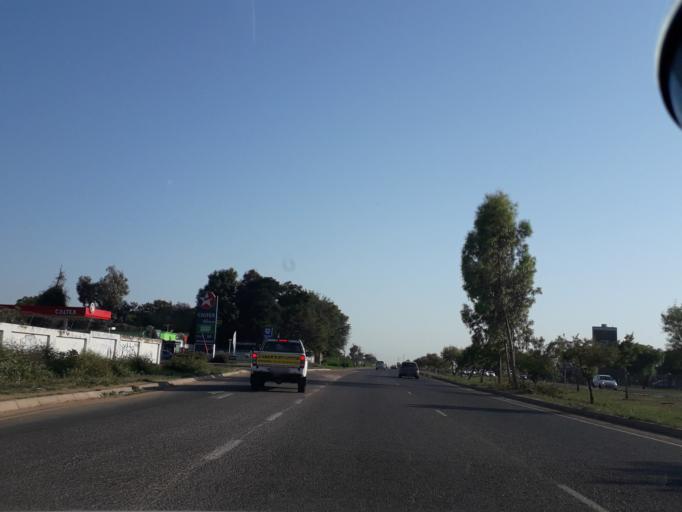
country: ZA
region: Gauteng
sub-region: City of Johannesburg Metropolitan Municipality
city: Roodepoort
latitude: -26.0886
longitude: 27.9281
